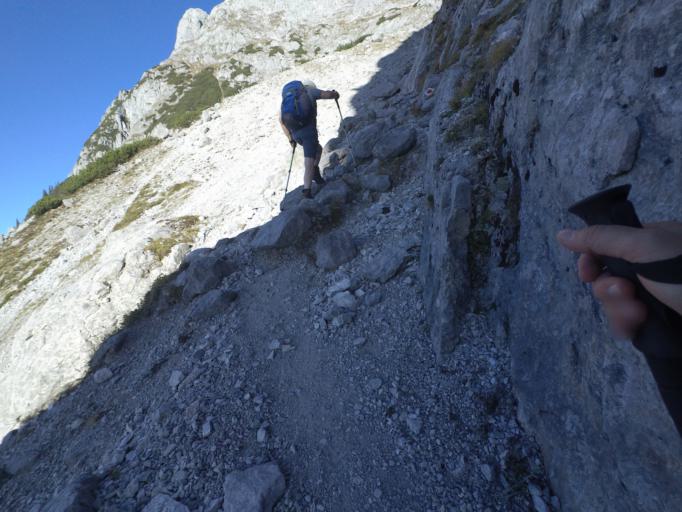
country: AT
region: Salzburg
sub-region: Politischer Bezirk Sankt Johann im Pongau
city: Werfenweng
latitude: 47.4927
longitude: 13.2332
